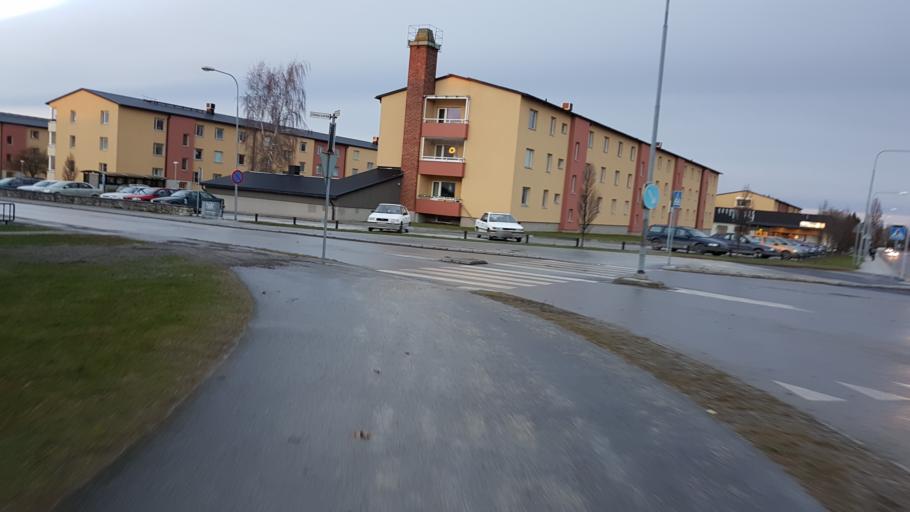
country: SE
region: Gotland
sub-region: Gotland
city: Visby
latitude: 57.6210
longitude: 18.2841
